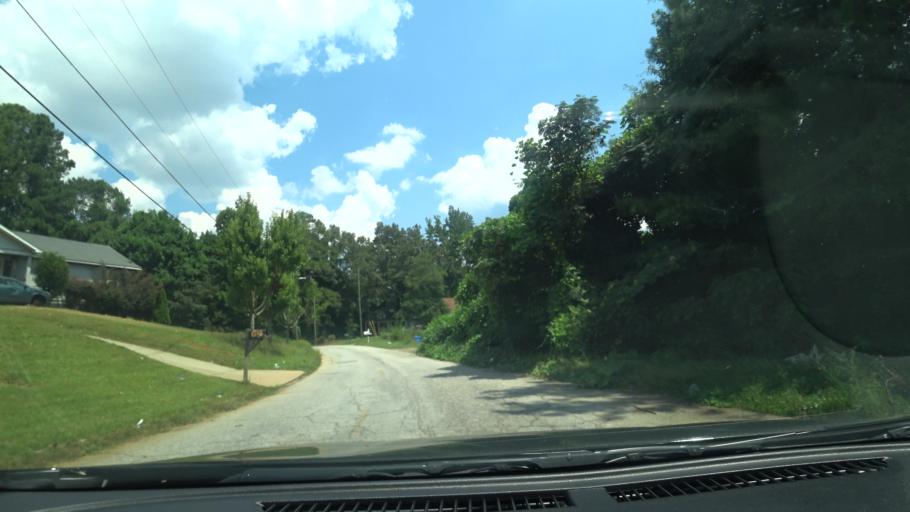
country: US
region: Georgia
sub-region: Fulton County
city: Hapeville
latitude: 33.6941
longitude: -84.3923
